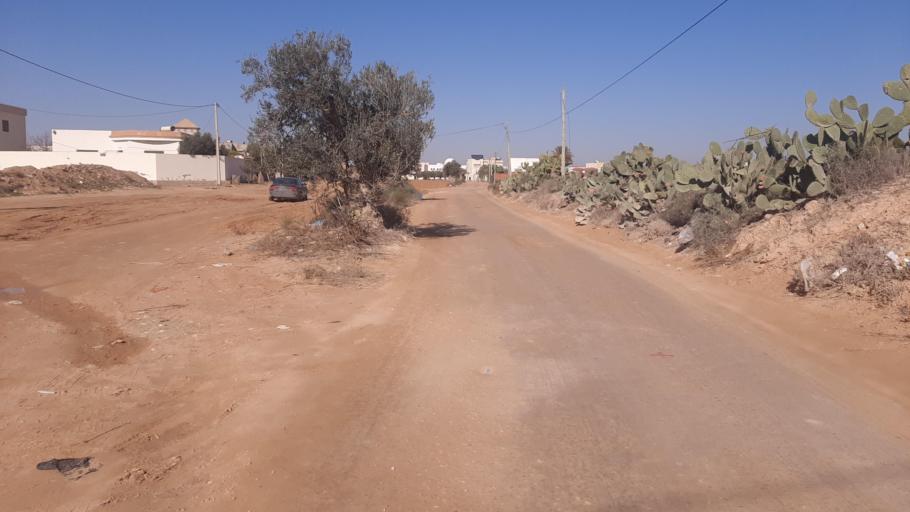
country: TN
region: Safaqis
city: Al Qarmadah
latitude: 34.7867
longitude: 10.8267
